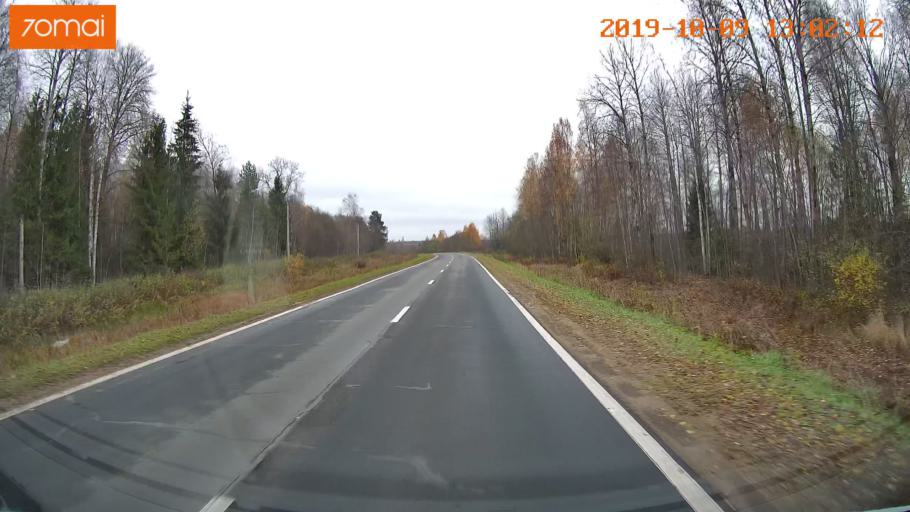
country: RU
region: Jaroslavl
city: Prechistoye
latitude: 58.3632
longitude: 40.4964
